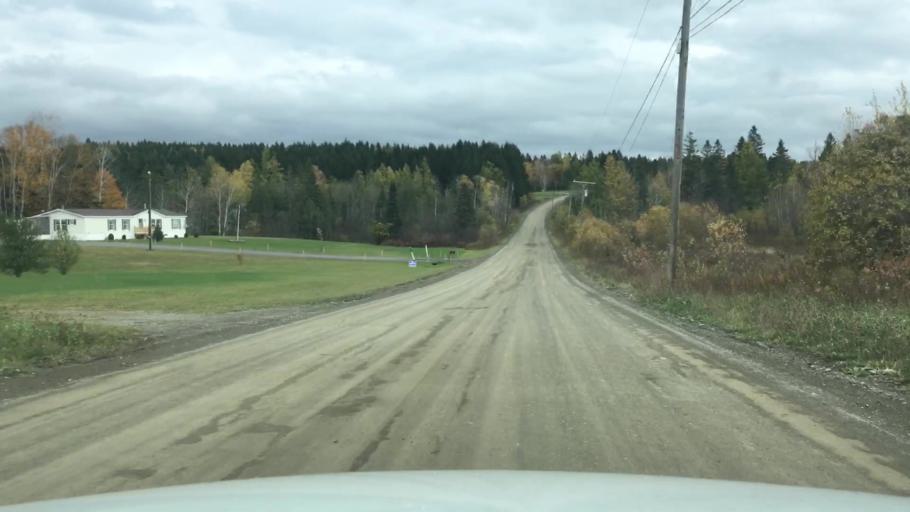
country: US
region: Maine
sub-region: Aroostook County
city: Easton
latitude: 46.5228
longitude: -67.8927
